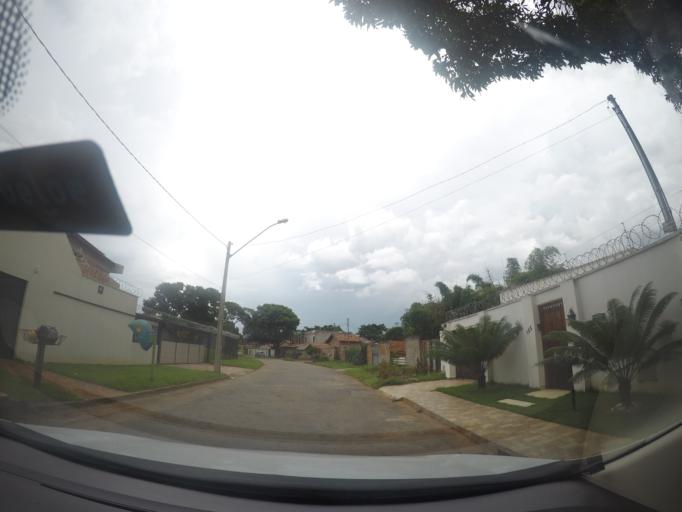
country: BR
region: Goias
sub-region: Goiania
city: Goiania
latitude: -16.6504
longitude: -49.2382
